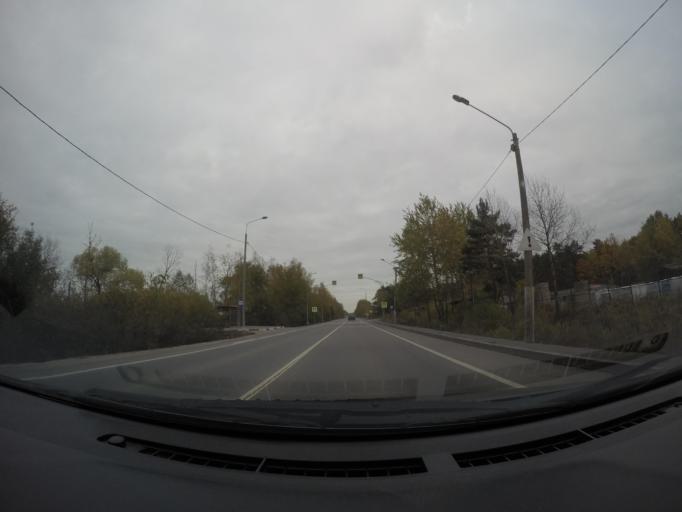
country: RU
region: Moskovskaya
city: Imeni Vorovskogo
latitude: 55.7219
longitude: 38.3753
